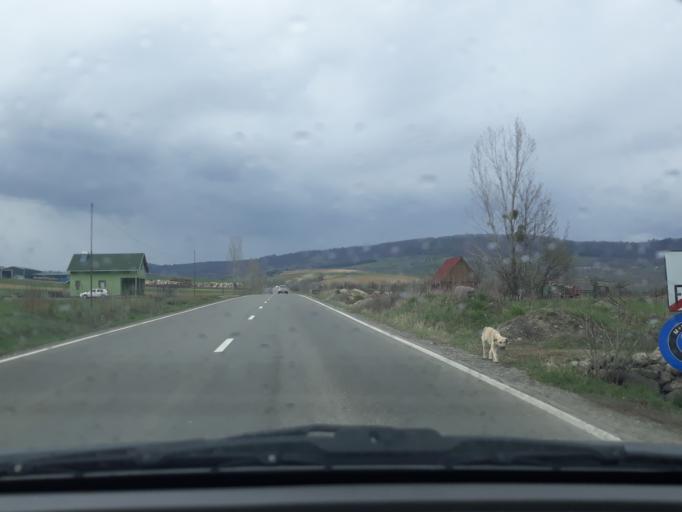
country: RO
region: Harghita
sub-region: Comuna Lupeni
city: Lupeni
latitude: 46.3867
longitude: 25.2172
